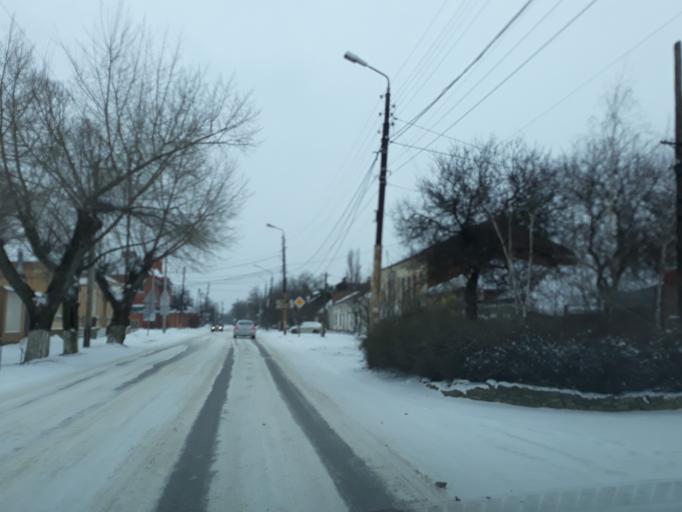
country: RU
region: Rostov
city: Taganrog
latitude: 47.2005
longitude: 38.9160
